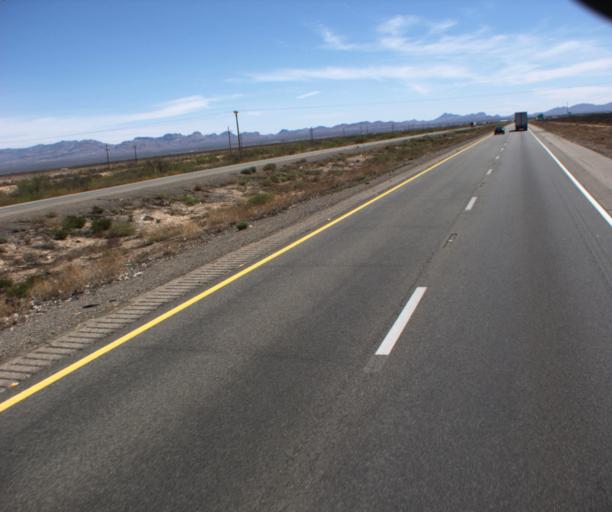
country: US
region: Arizona
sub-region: Cochise County
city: Willcox
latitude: 32.2784
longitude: -109.2721
